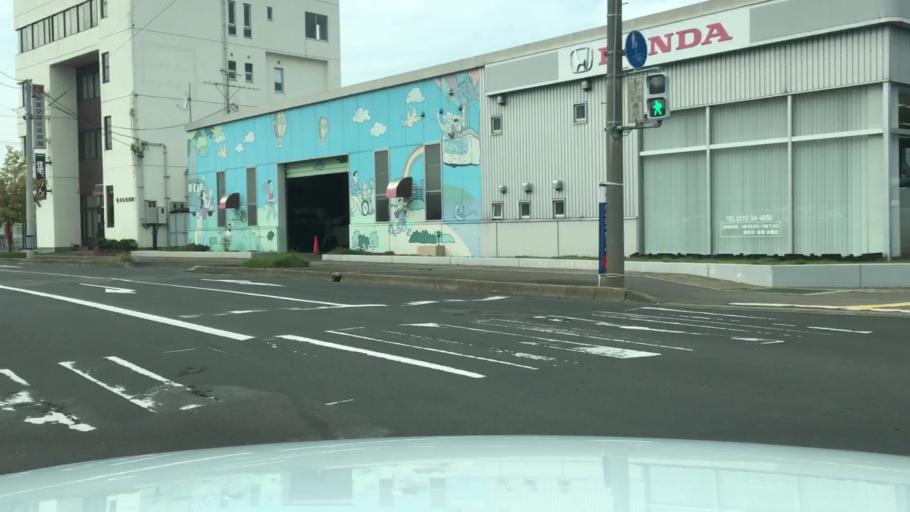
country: JP
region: Aomori
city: Hirosaki
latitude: 40.6170
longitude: 140.4860
